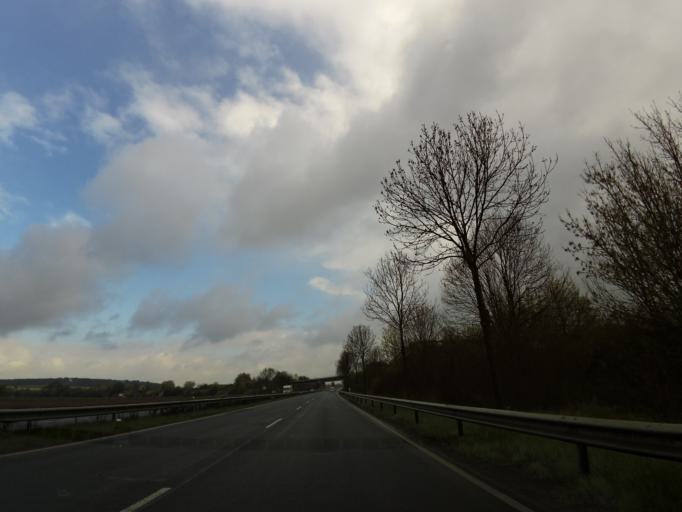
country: DE
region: Lower Saxony
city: Bovenden
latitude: 51.5676
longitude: 9.9201
